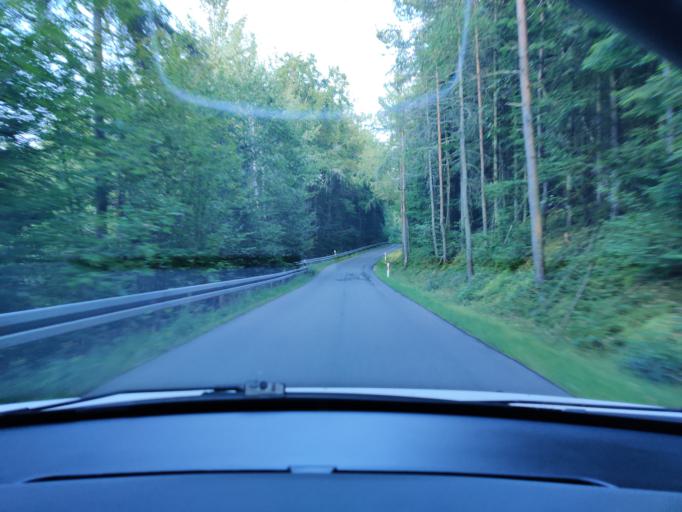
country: DE
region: Bavaria
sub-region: Upper Palatinate
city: Nabburg
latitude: 49.4282
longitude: 12.1817
